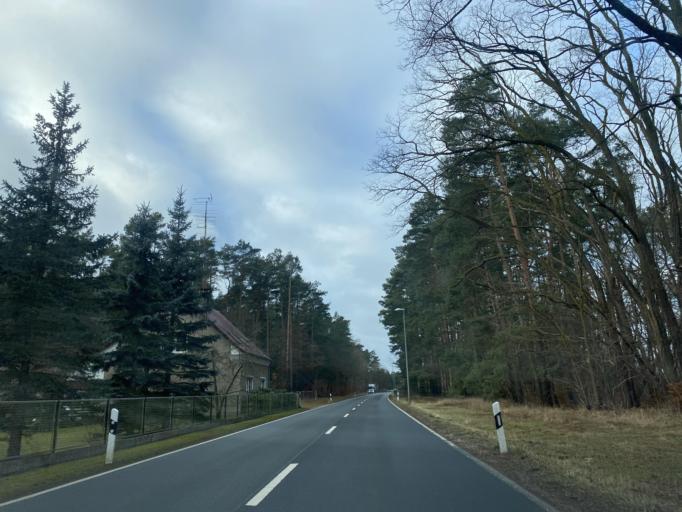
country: PL
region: Lubusz
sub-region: Powiat zarski
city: Przewoz
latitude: 51.4804
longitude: 14.8579
